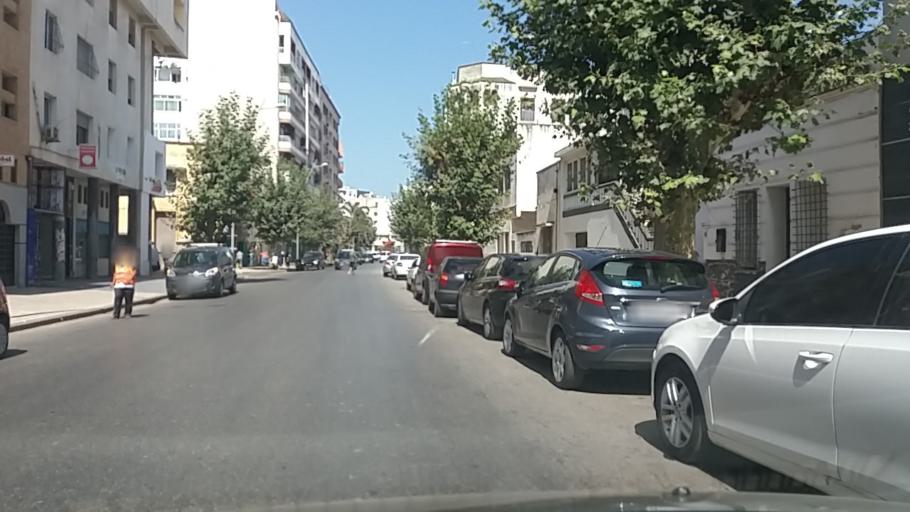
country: MA
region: Gharb-Chrarda-Beni Hssen
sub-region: Kenitra Province
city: Kenitra
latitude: 34.2578
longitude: -6.5851
